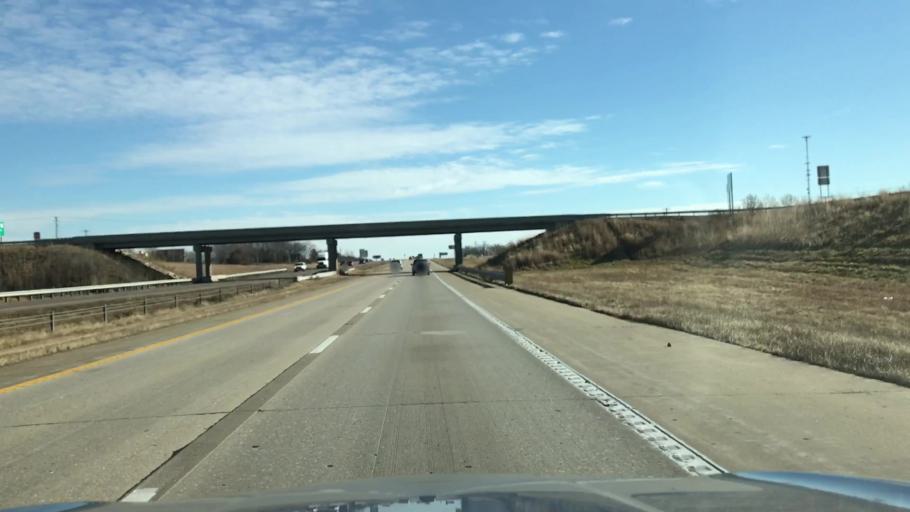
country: US
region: Missouri
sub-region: Callaway County
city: Fulton
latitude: 38.9338
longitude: -91.8064
